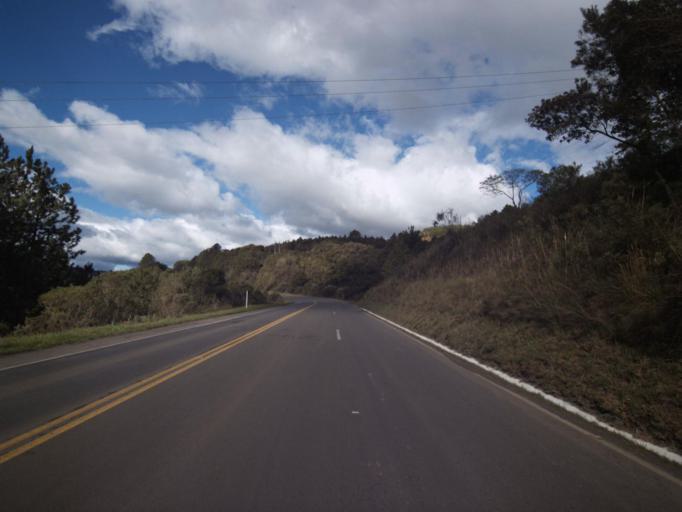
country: BR
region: Santa Catarina
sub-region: Joacaba
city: Joacaba
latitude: -27.0570
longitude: -51.6853
